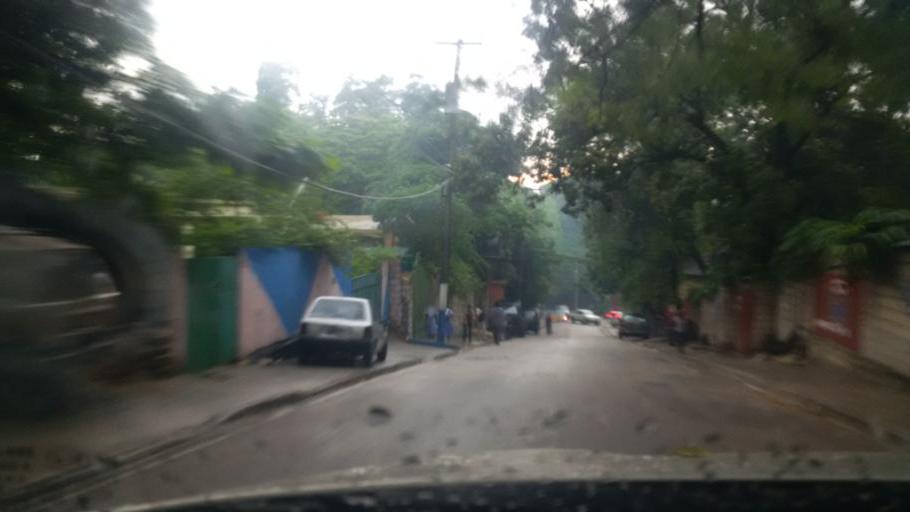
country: HT
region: Ouest
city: Port-au-Prince
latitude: 18.5296
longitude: -72.3221
